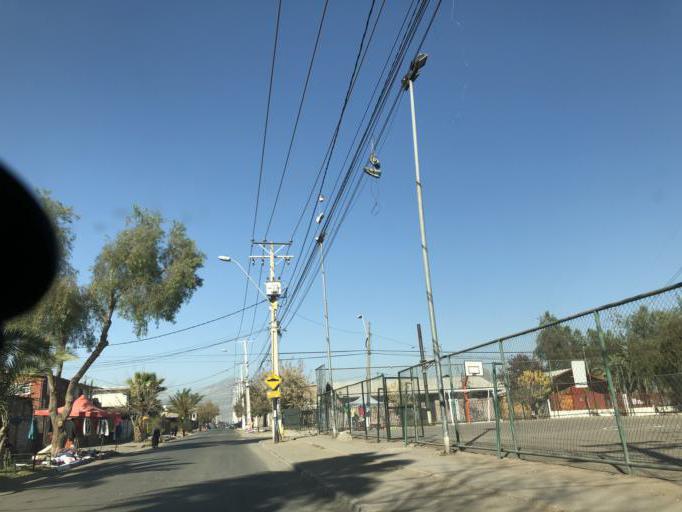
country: CL
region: Santiago Metropolitan
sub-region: Provincia de Santiago
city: La Pintana
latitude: -33.6192
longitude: -70.6179
